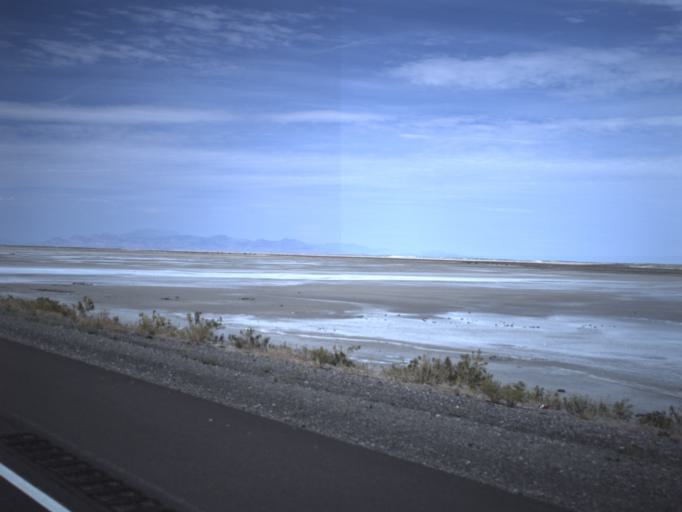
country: US
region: Utah
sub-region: Tooele County
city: Wendover
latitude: 40.7281
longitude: -113.2986
